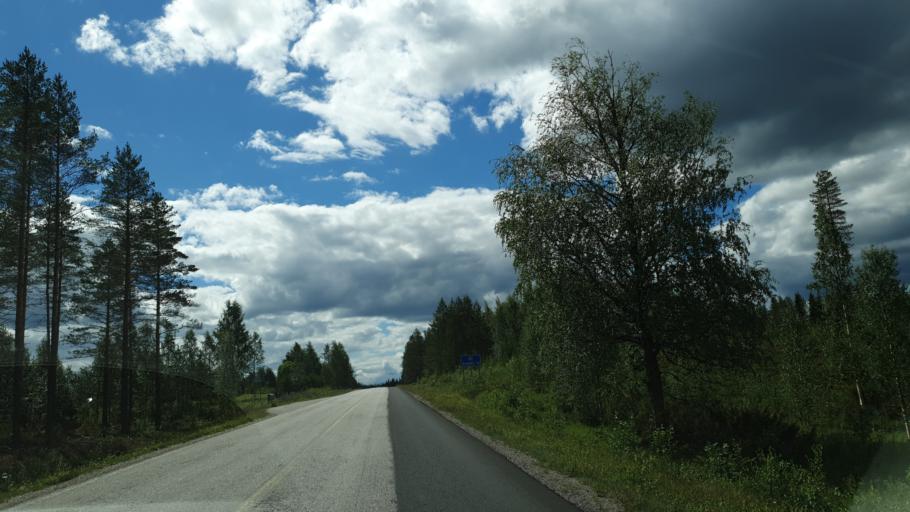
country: FI
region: Kainuu
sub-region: Kehys-Kainuu
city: Kuhmo
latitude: 63.9242
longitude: 29.5529
